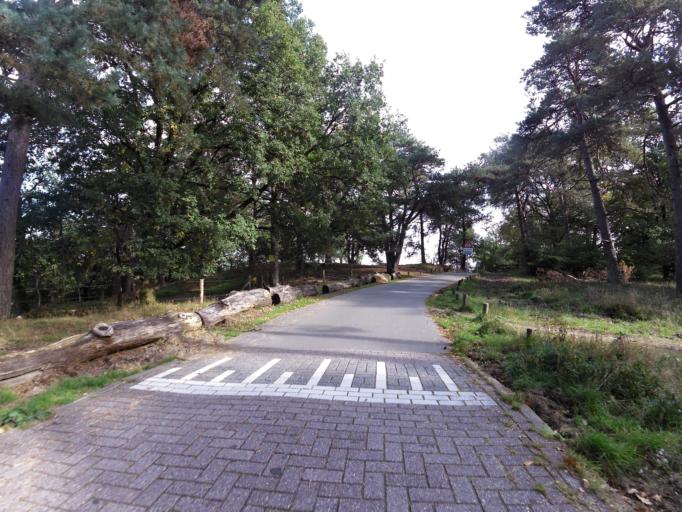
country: NL
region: Gelderland
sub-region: Gemeente Rheden
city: Rheden
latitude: 52.0258
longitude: 6.0040
